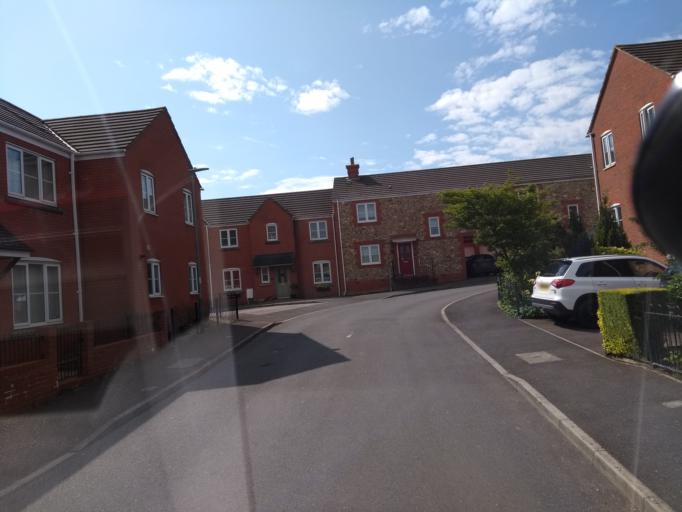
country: GB
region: England
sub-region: Somerset
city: Chard
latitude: 50.8694
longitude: -2.9701
